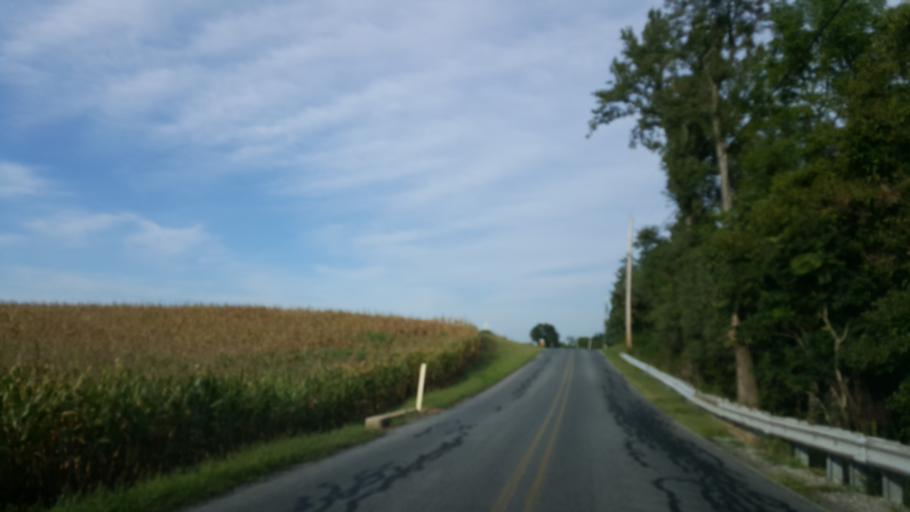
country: US
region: Pennsylvania
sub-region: Lebanon County
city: Campbelltown
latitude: 40.2645
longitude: -76.5703
